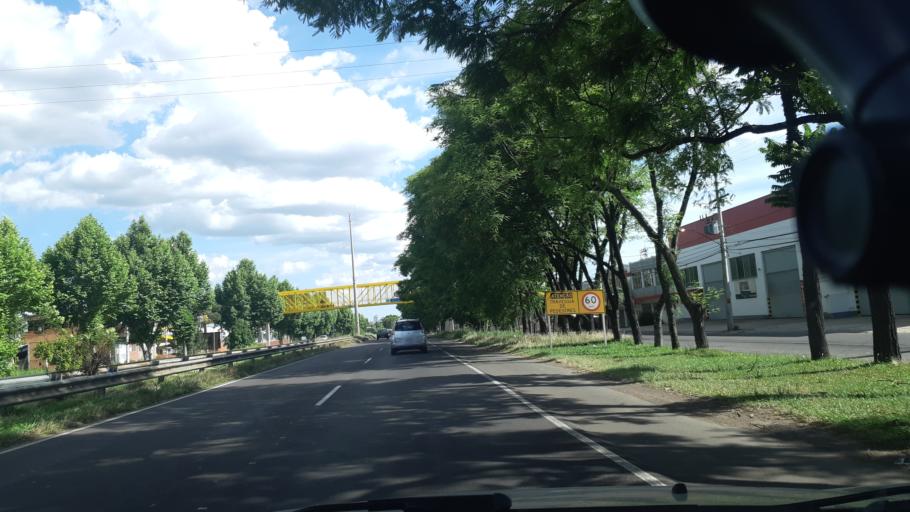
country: BR
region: Rio Grande do Sul
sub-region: Novo Hamburgo
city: Novo Hamburgo
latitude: -29.6618
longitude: -51.1439
